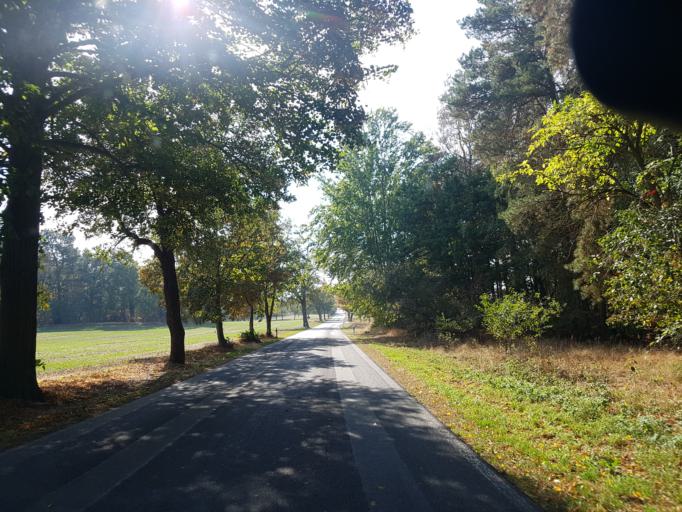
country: DE
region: Brandenburg
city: Hohenbucko
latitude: 51.7142
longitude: 13.4904
